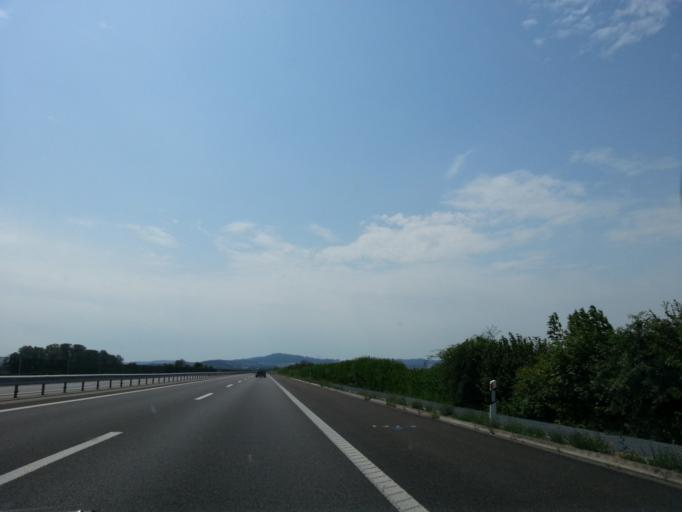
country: CH
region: Vaud
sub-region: Broye-Vully District
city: Payerne
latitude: 46.8542
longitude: 6.9437
